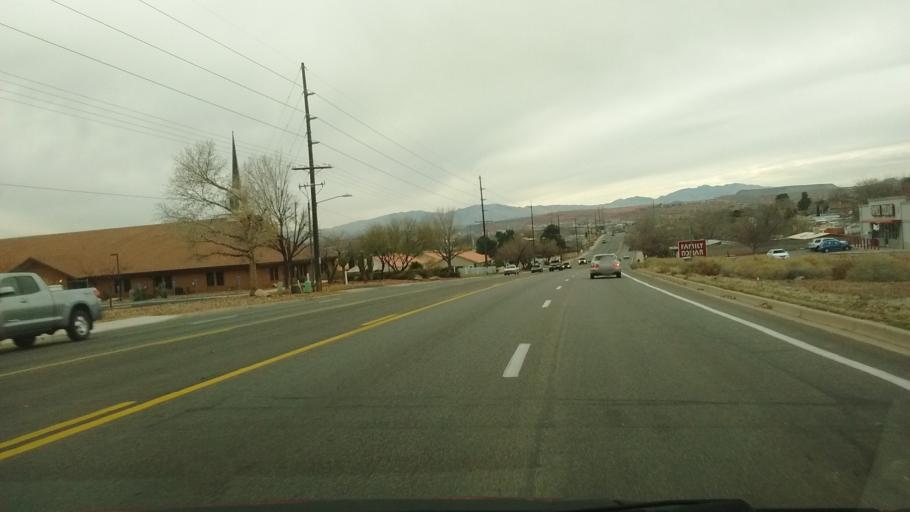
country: US
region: Utah
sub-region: Washington County
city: Washington
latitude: 37.1303
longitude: -113.4985
